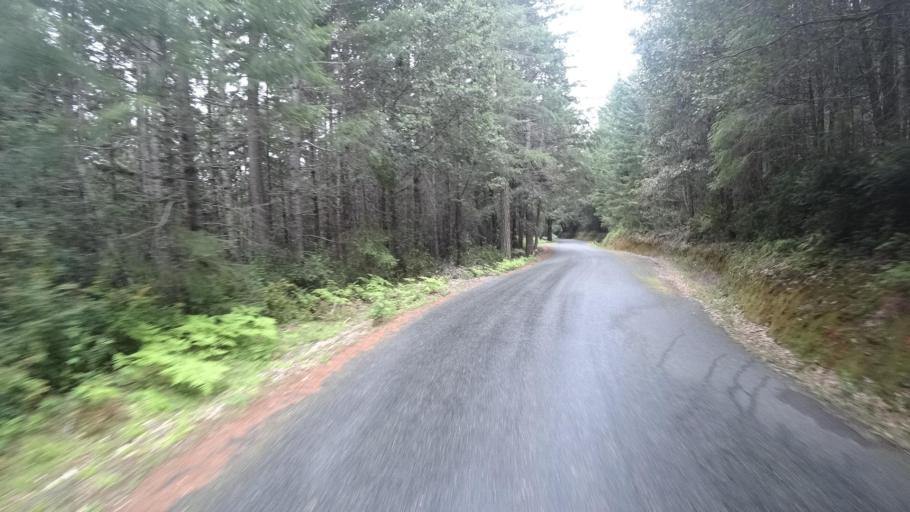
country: US
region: California
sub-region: Humboldt County
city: Willow Creek
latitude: 41.2011
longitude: -123.7649
